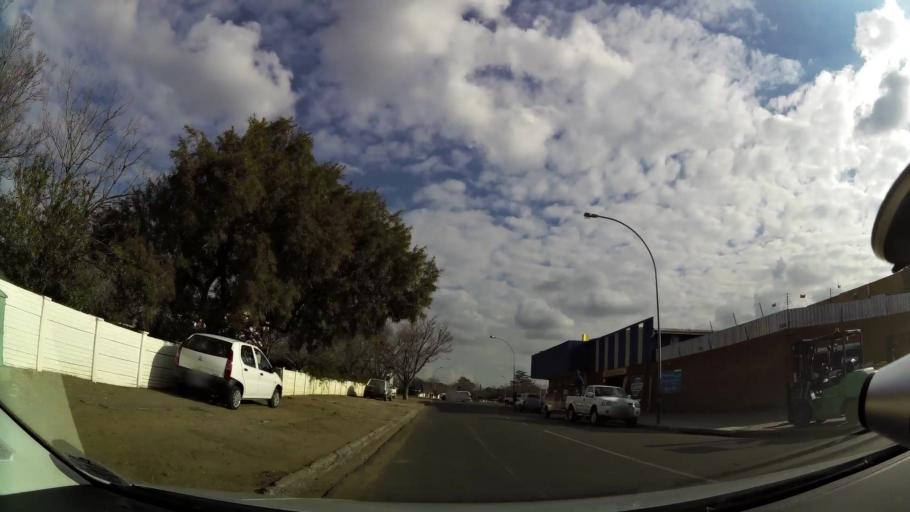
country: ZA
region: Orange Free State
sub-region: Mangaung Metropolitan Municipality
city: Bloemfontein
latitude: -29.0818
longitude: 26.2153
